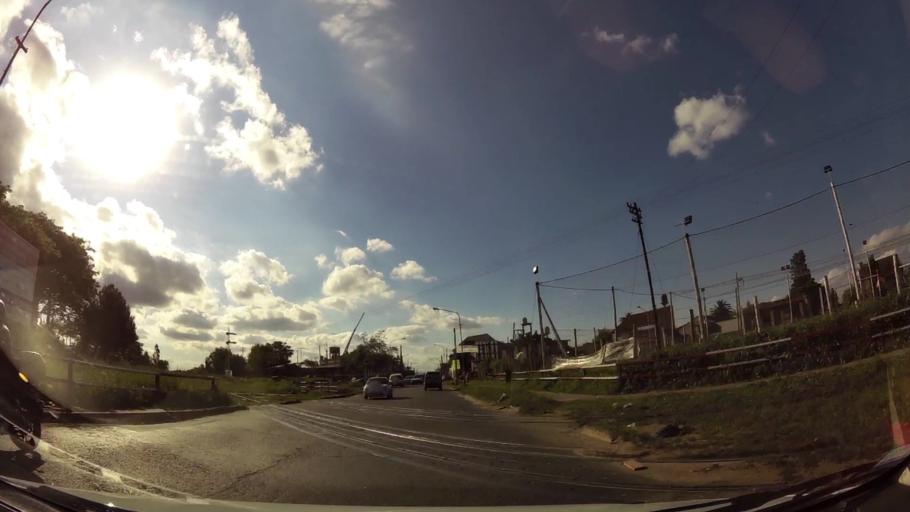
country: AR
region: Buenos Aires
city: San Justo
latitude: -34.7038
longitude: -58.5928
